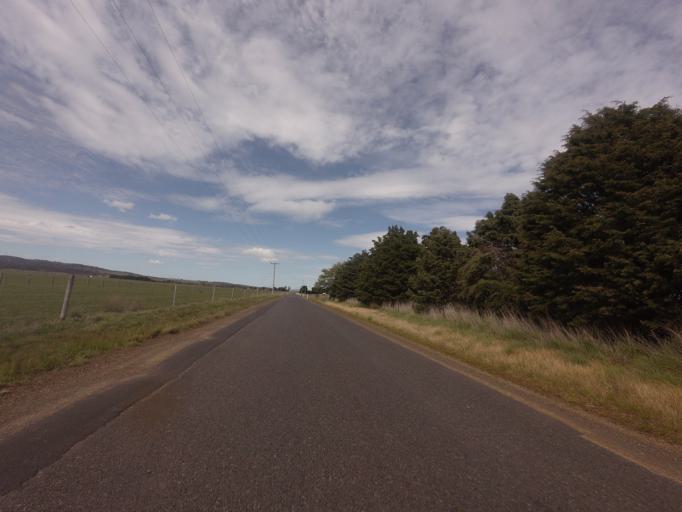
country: AU
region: Tasmania
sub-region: Northern Midlands
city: Evandale
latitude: -41.8124
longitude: 147.2906
